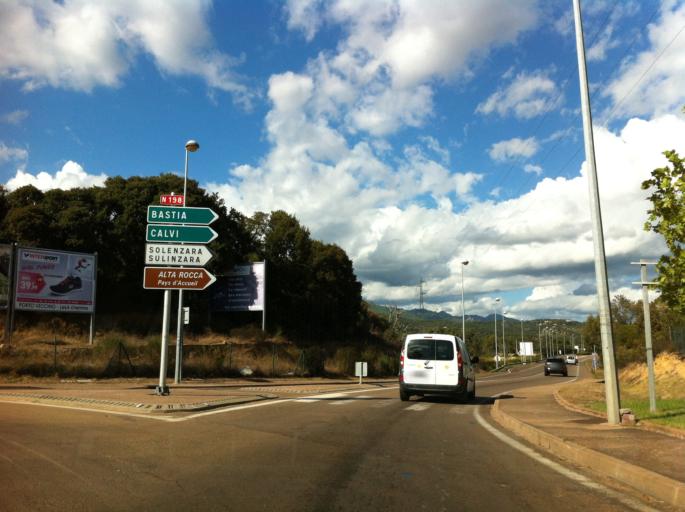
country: FR
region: Corsica
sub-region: Departement de la Corse-du-Sud
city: Porto-Vecchio
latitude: 41.5982
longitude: 9.2671
